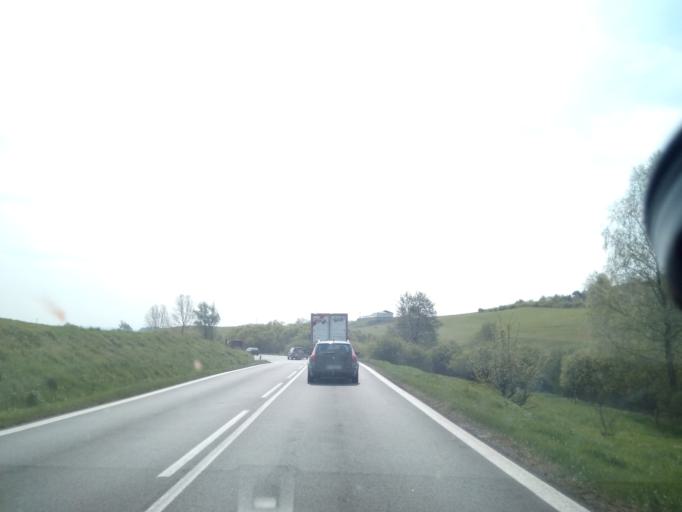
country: SK
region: Presovsky
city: Giraltovce
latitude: 49.0418
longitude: 21.4460
